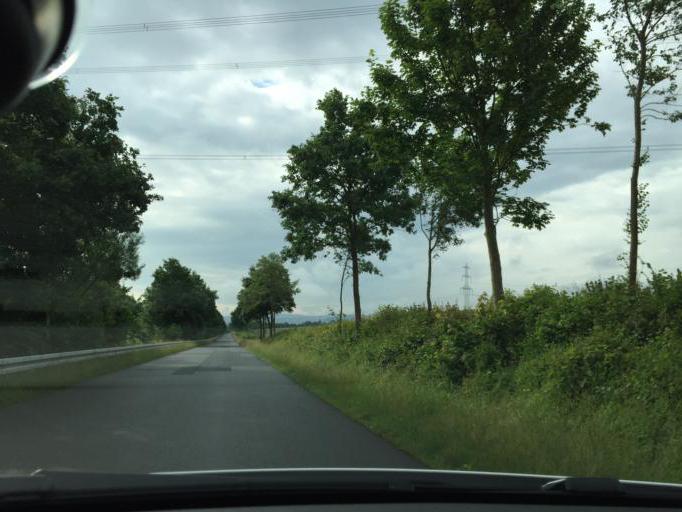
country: DE
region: Lower Saxony
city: Hehlen
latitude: 52.0319
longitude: 9.4053
